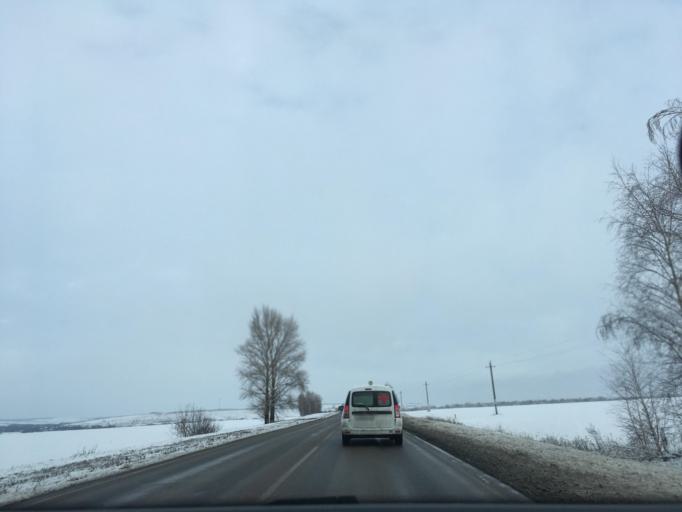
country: UA
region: Luhansk
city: Lozno-Oleksandrivka
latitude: 49.9527
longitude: 38.9582
